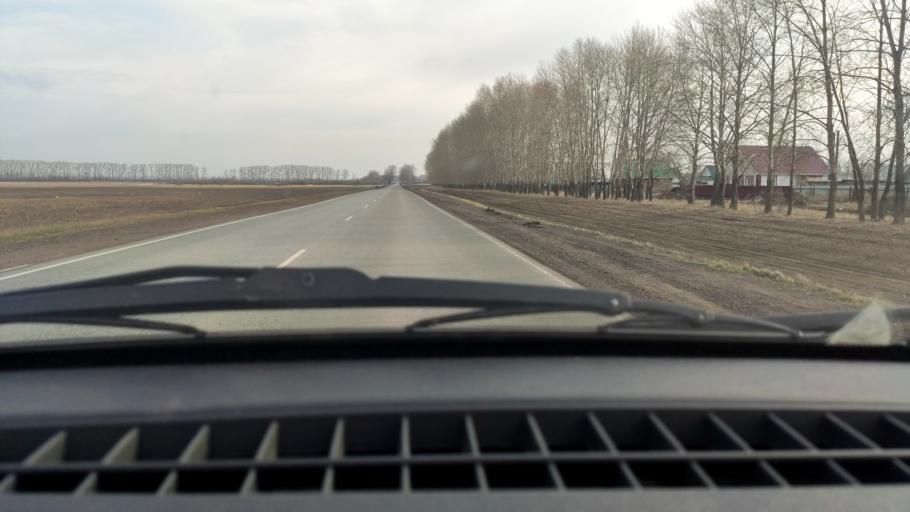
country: RU
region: Bashkortostan
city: Davlekanovo
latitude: 54.3942
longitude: 55.2063
